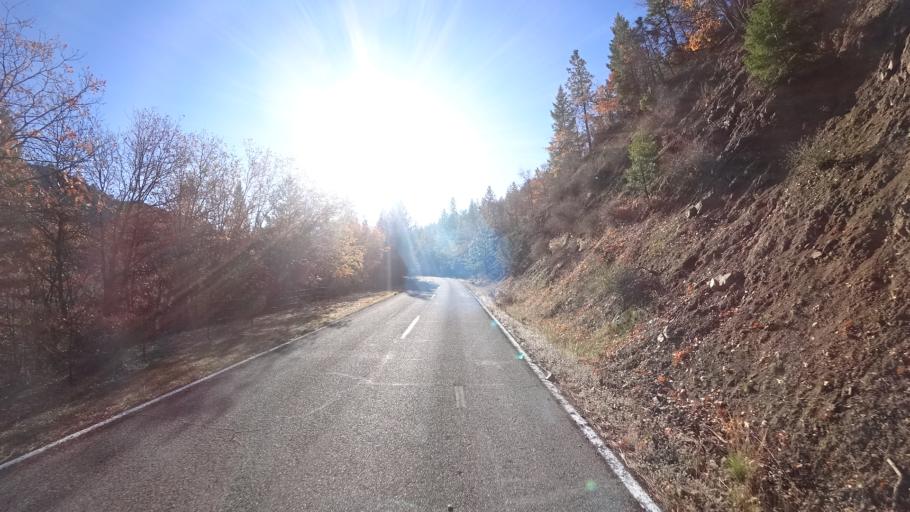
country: US
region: California
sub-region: Siskiyou County
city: Yreka
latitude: 41.9080
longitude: -122.8354
